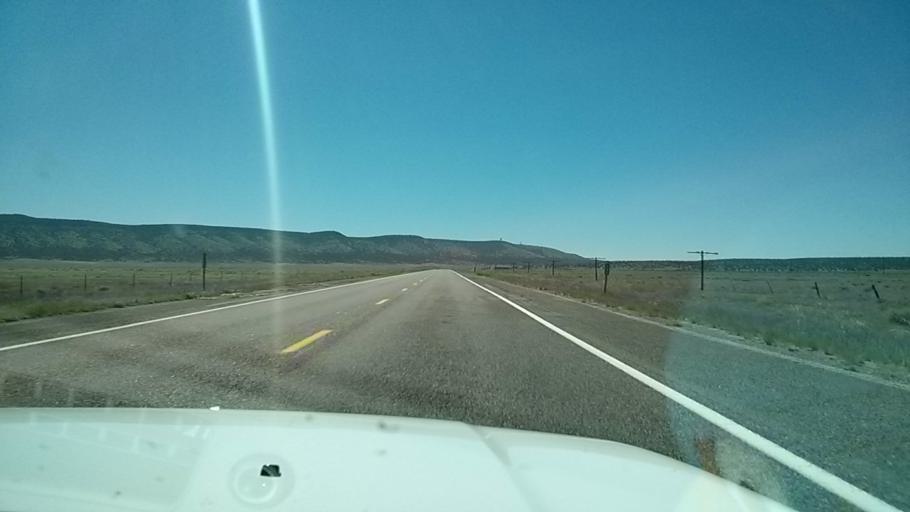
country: US
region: Arizona
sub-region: Mohave County
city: Peach Springs
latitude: 35.3965
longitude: -113.0094
